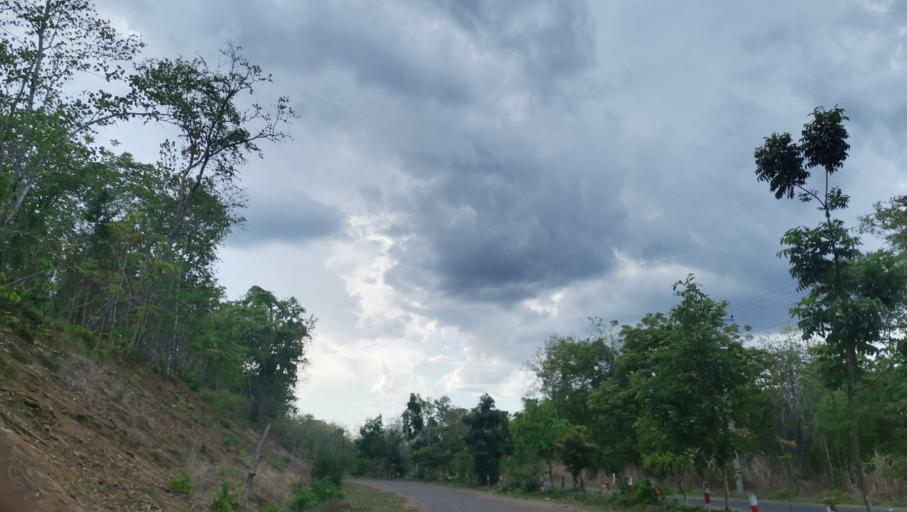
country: MM
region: Magway
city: Minbu
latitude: 20.1043
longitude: 94.5477
